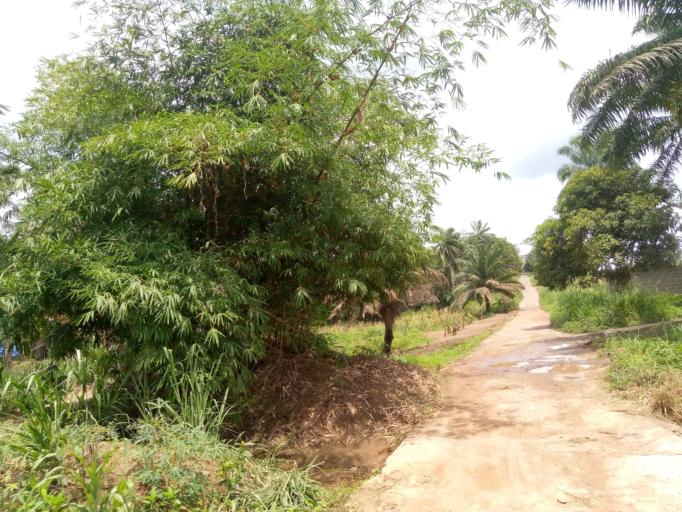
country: SL
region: Western Area
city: Waterloo
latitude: 8.3460
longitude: -12.9844
